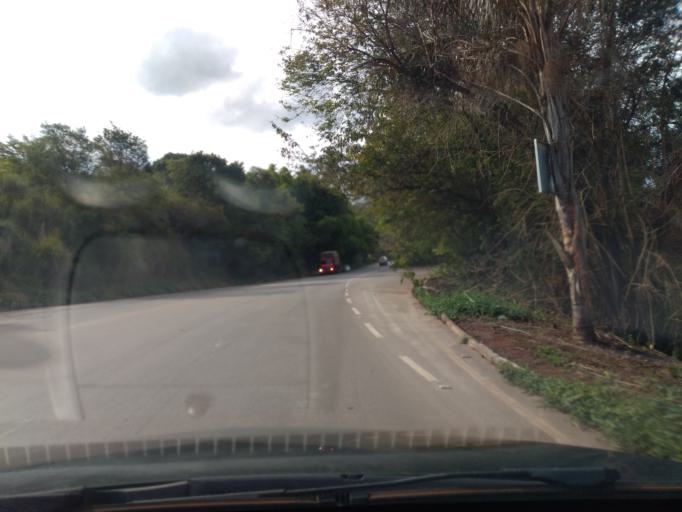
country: BR
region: Minas Gerais
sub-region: Varginha
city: Varginha
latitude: -21.6110
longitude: -45.4317
